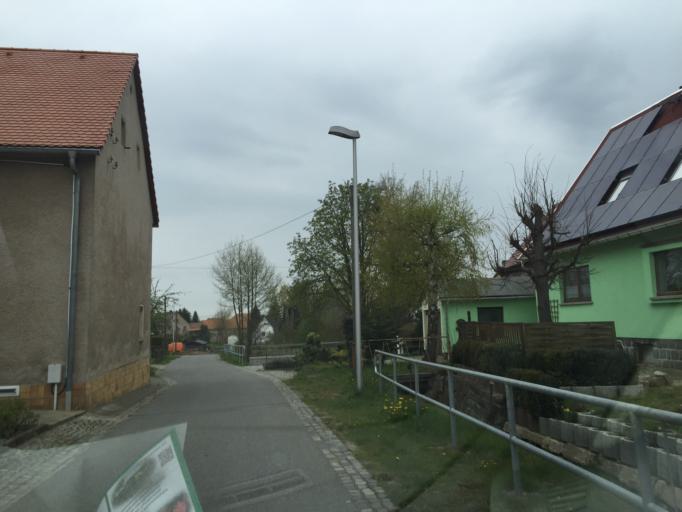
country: DE
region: Saxony
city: Lobau
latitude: 51.0726
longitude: 14.6863
